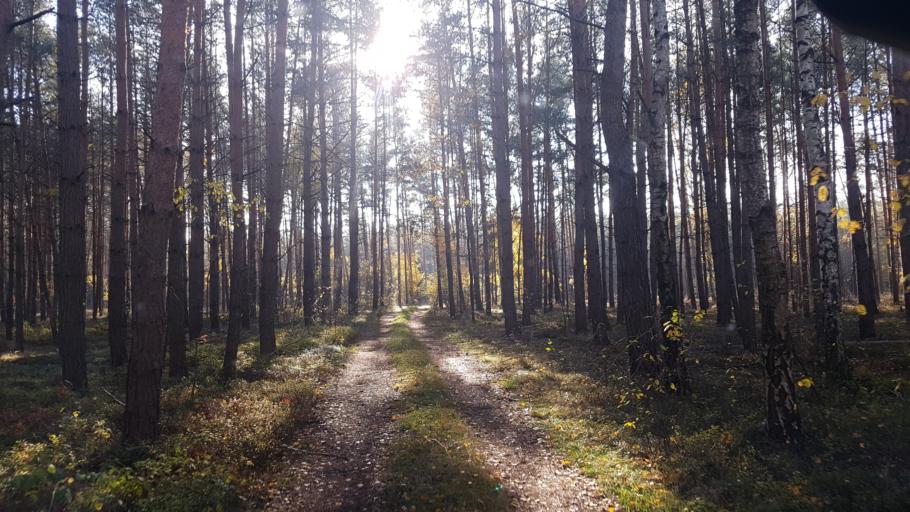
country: DE
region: Brandenburg
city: Schonborn
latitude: 51.6629
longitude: 13.4989
